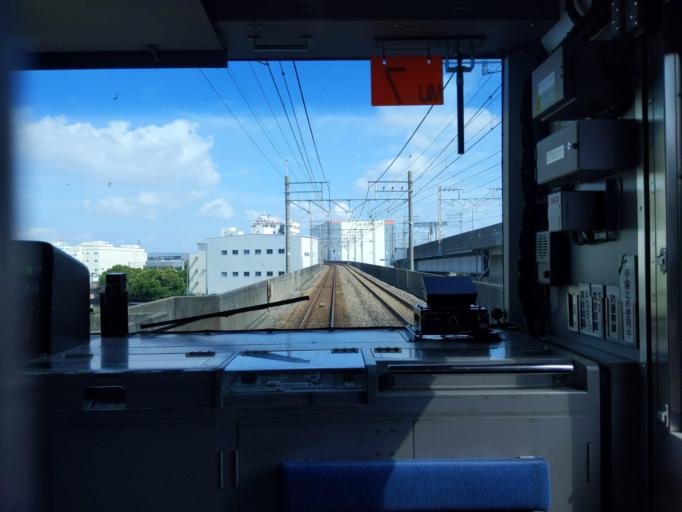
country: JP
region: Chiba
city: Funabashi
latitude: 35.6889
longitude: 139.9527
